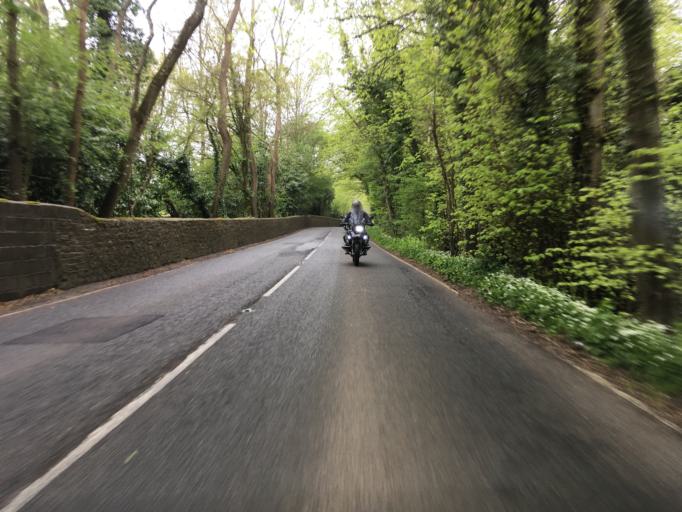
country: GB
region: England
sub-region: Bath and North East Somerset
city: Stanton Drew
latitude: 51.3391
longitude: -2.5799
